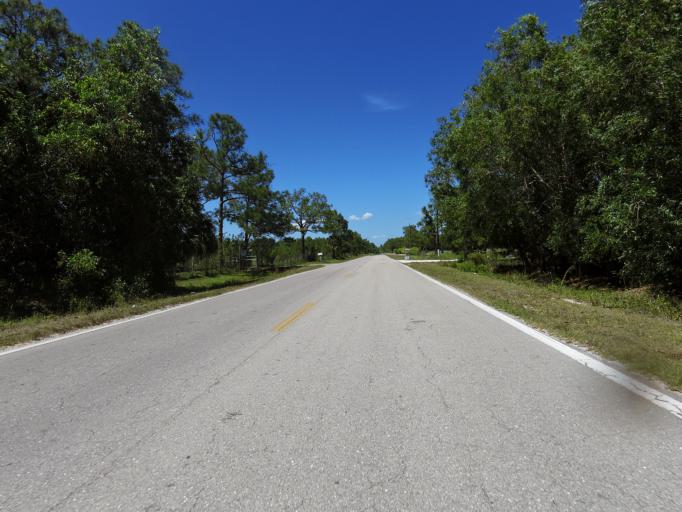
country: US
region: Florida
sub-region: Collier County
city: Orangetree
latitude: 26.3685
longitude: -81.5876
